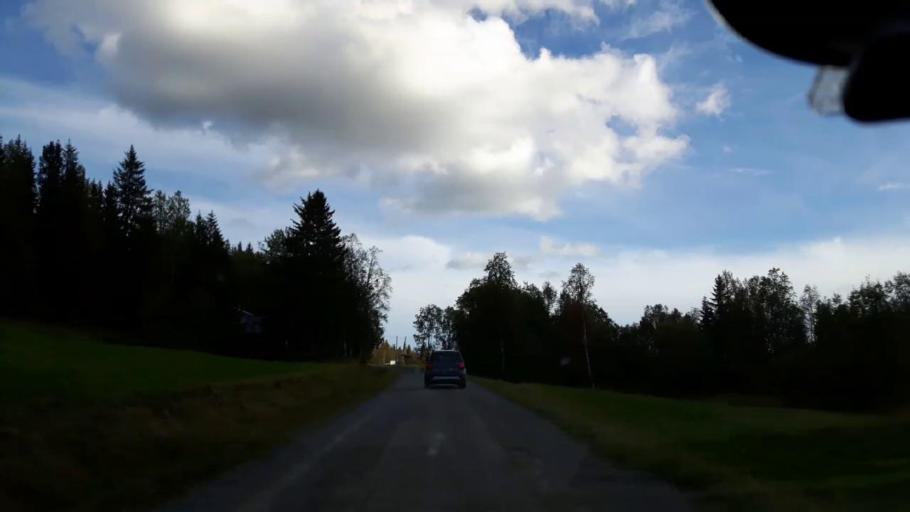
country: SE
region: Jaemtland
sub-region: Ragunda Kommun
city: Hammarstrand
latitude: 63.4138
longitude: 16.0818
